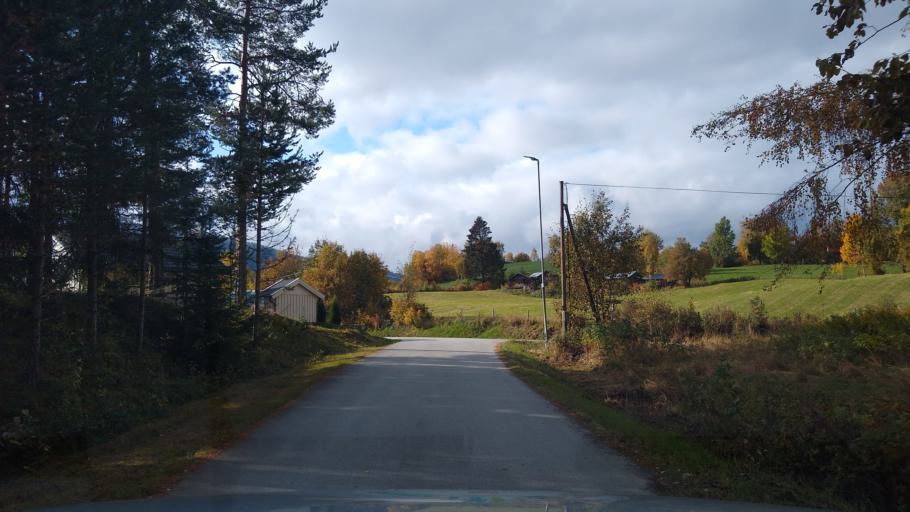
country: NO
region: Oppland
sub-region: Ringebu
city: Ringebu
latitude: 61.5411
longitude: 10.1347
